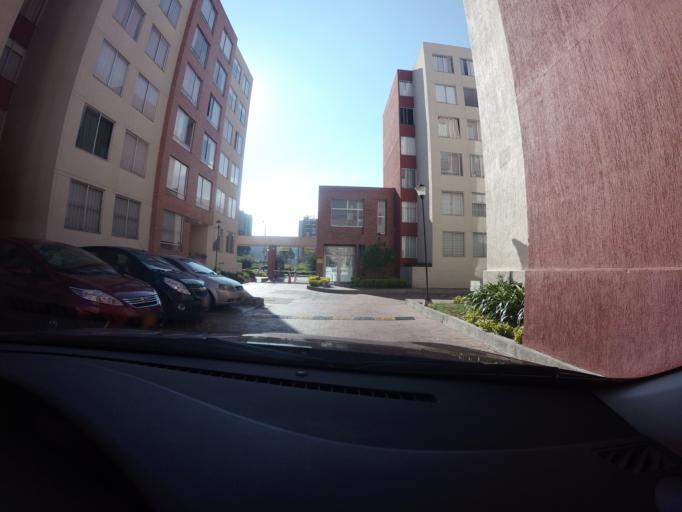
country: CO
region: Cundinamarca
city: Cota
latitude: 4.7417
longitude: -74.0619
